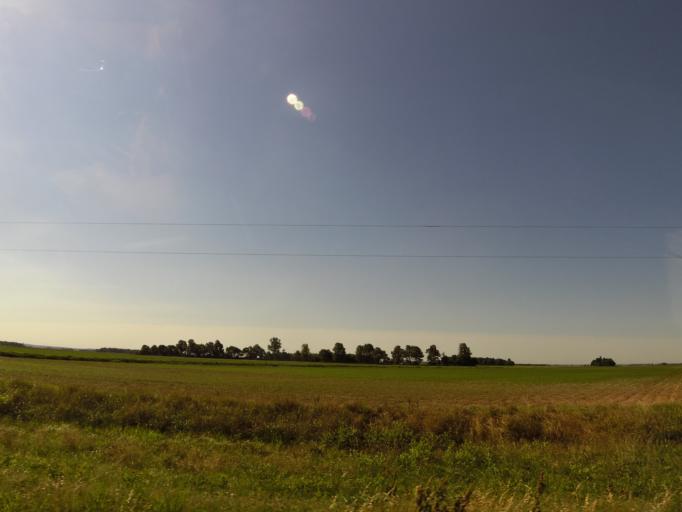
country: US
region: Arkansas
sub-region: Clay County
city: Corning
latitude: 36.4058
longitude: -90.5026
